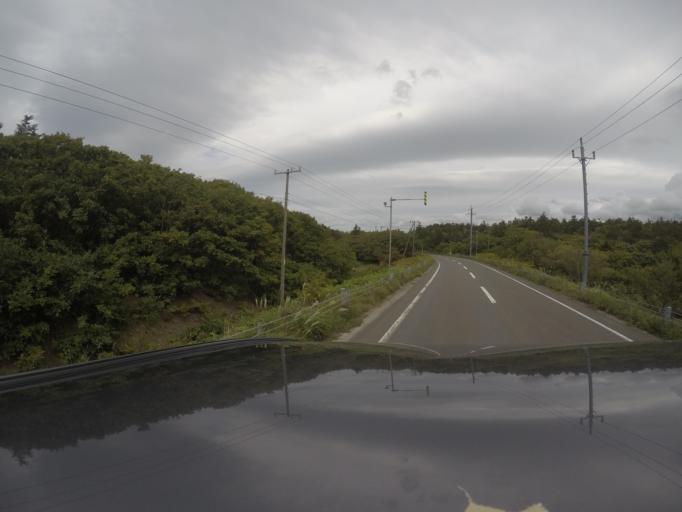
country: JP
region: Hokkaido
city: Makubetsu
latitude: 44.9977
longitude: 141.6955
